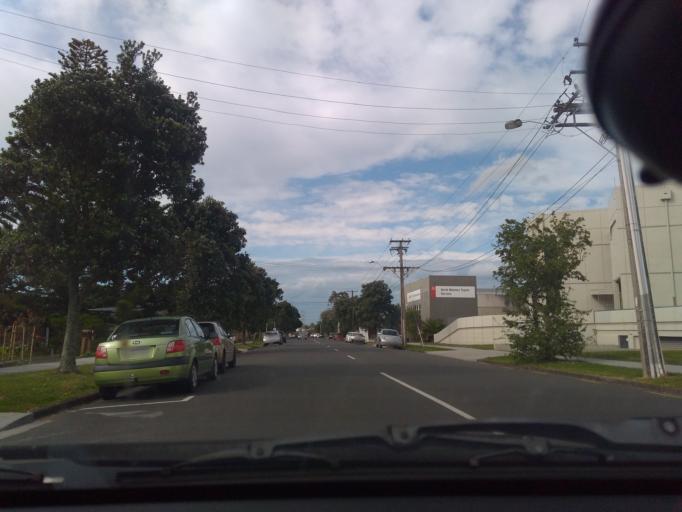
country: NZ
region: Auckland
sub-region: Auckland
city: Waitakere
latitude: -36.9070
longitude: 174.6829
